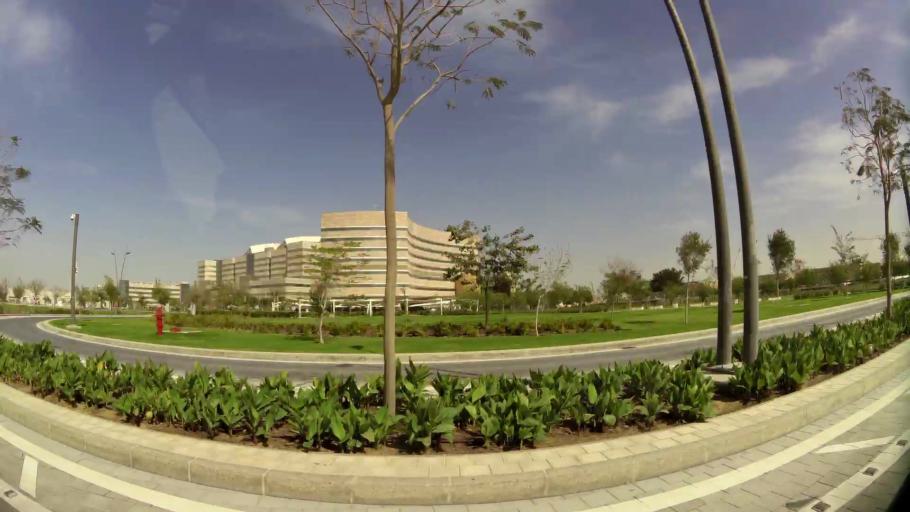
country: QA
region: Baladiyat ar Rayyan
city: Ar Rayyan
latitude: 25.3220
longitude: 51.4408
